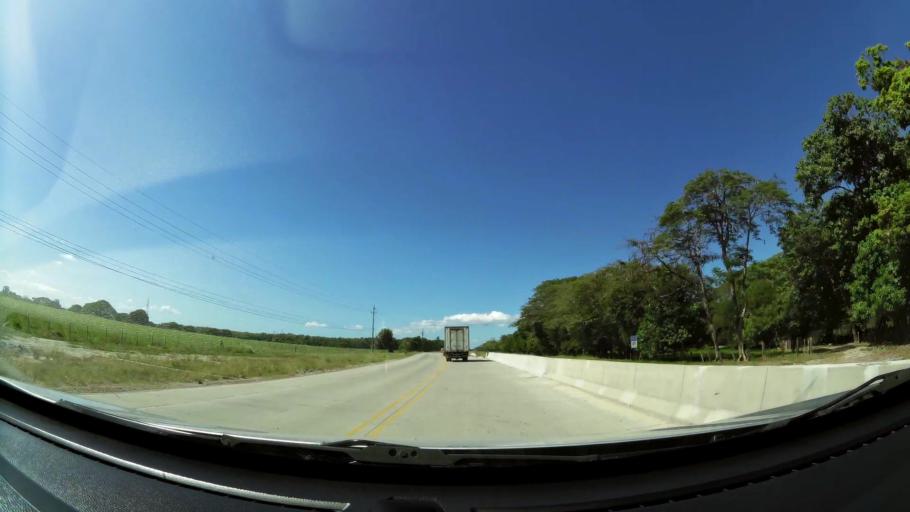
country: CR
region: Guanacaste
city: Liberia
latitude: 10.5723
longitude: -85.3965
